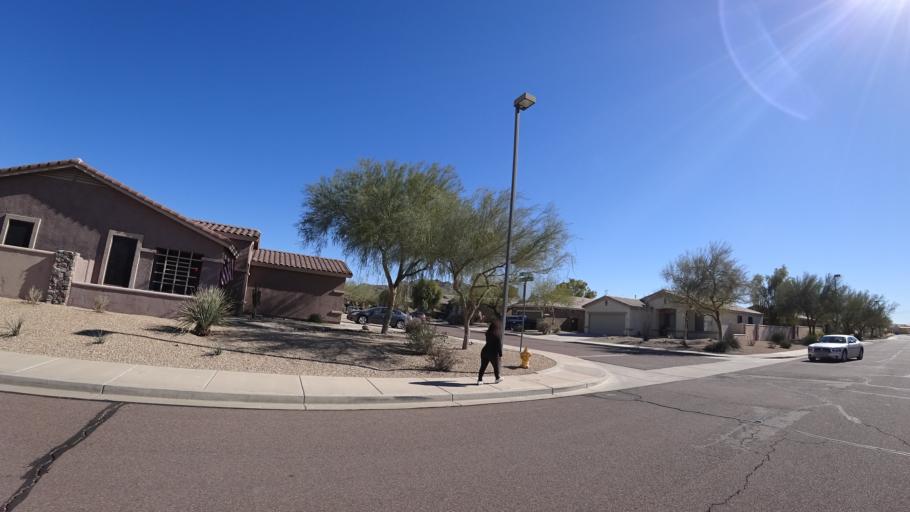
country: US
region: Arizona
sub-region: Maricopa County
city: Goodyear
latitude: 33.3509
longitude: -112.4268
